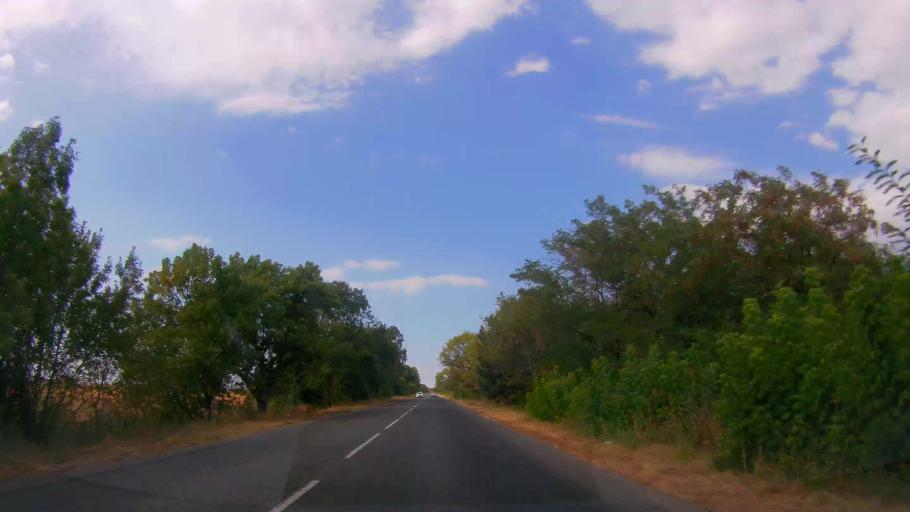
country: BG
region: Burgas
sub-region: Obshtina Aytos
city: Aytos
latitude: 42.6891
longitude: 27.1544
